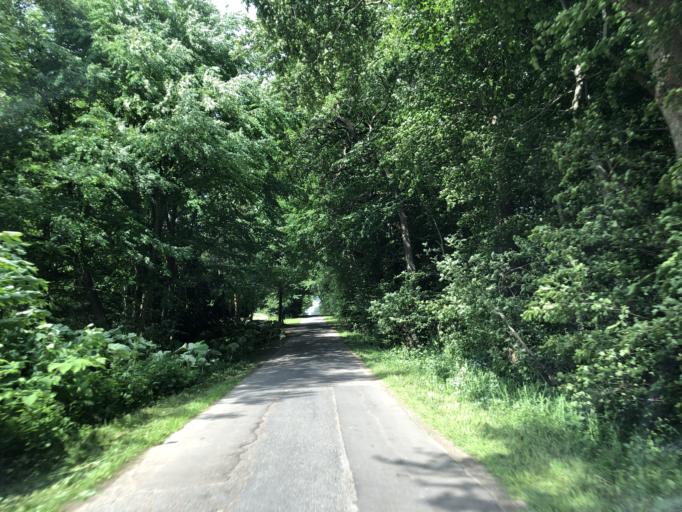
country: DK
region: Central Jutland
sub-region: Odder Kommune
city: Odder
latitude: 55.9706
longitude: 10.0936
